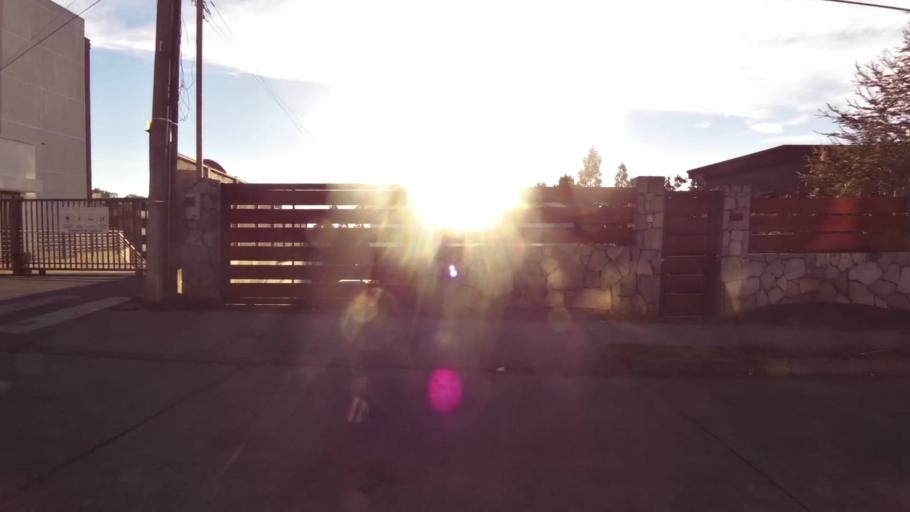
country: CL
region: Biobio
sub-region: Provincia de Concepcion
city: Concepcion
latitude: -36.8554
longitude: -73.0925
